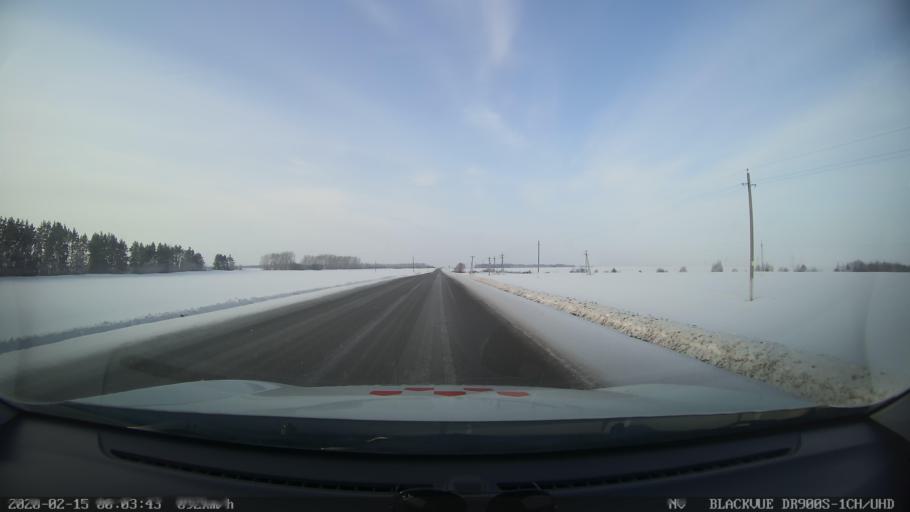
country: RU
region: Tatarstan
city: Kuybyshevskiy Zaton
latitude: 55.3747
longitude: 48.9938
